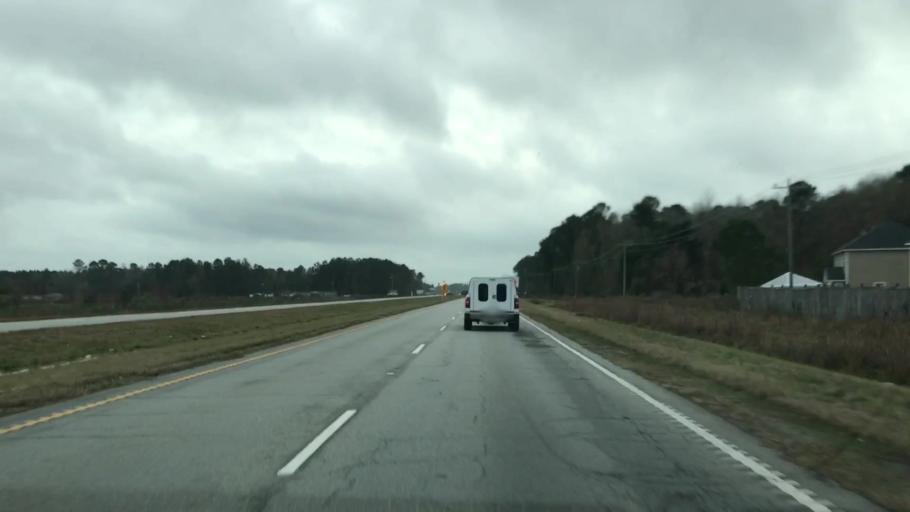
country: US
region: South Carolina
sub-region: Berkeley County
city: Moncks Corner
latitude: 33.1518
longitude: -80.0330
